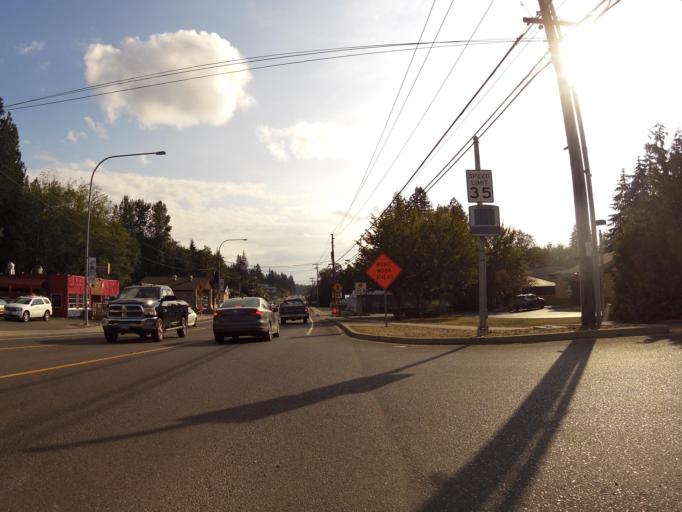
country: US
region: Washington
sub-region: Mason County
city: Belfair
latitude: 47.4509
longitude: -122.8276
